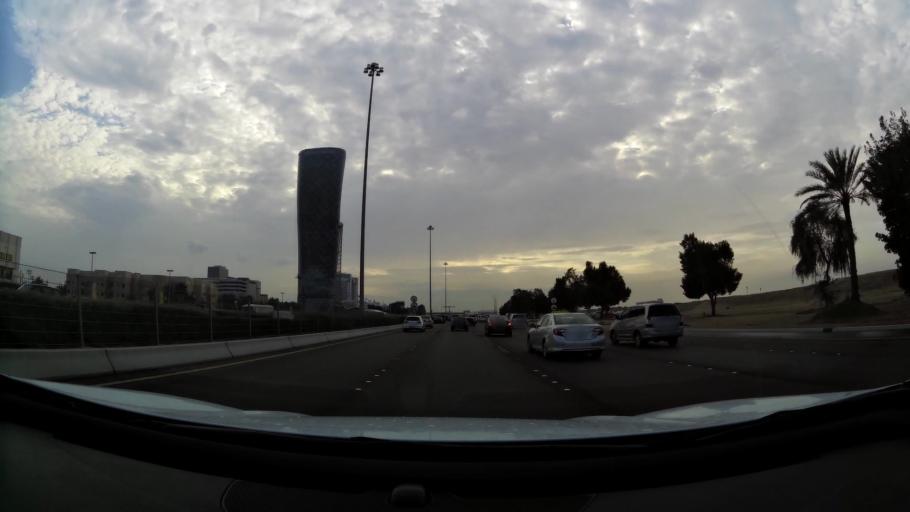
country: AE
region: Abu Dhabi
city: Abu Dhabi
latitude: 24.4187
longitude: 54.4304
